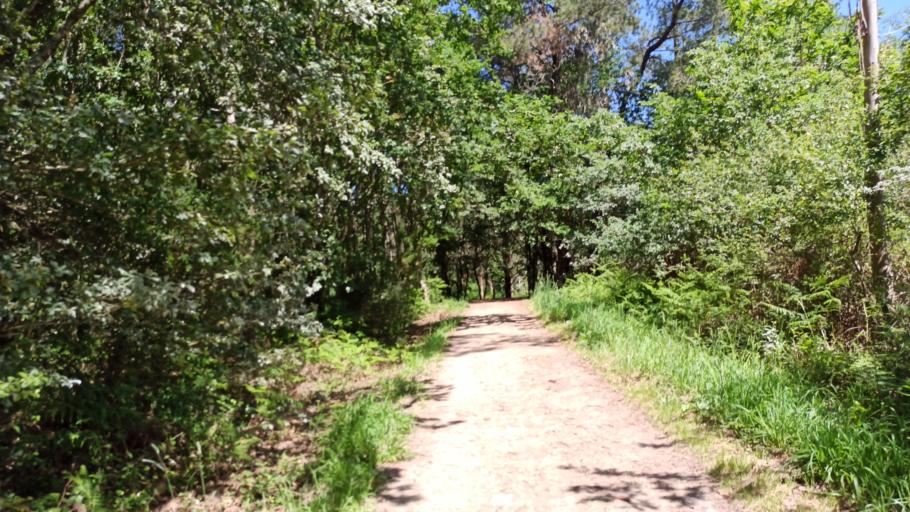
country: ES
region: Galicia
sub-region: Provincia da Coruna
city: Negreira
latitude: 42.9157
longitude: -8.7307
